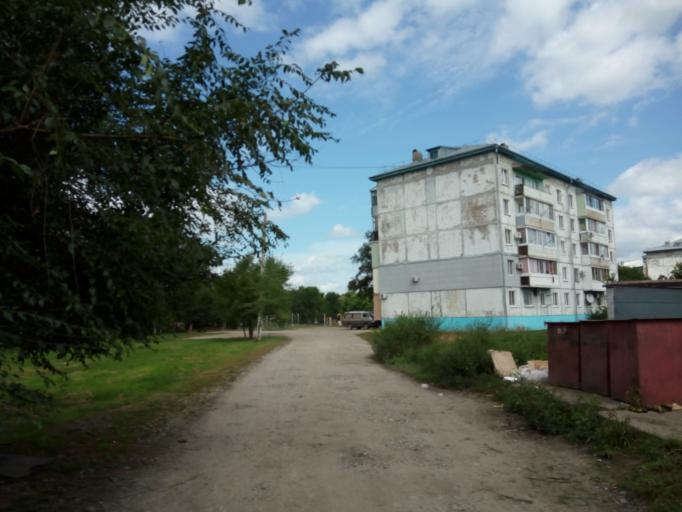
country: RU
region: Primorskiy
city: Dal'nerechensk
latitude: 45.9438
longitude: 133.8163
